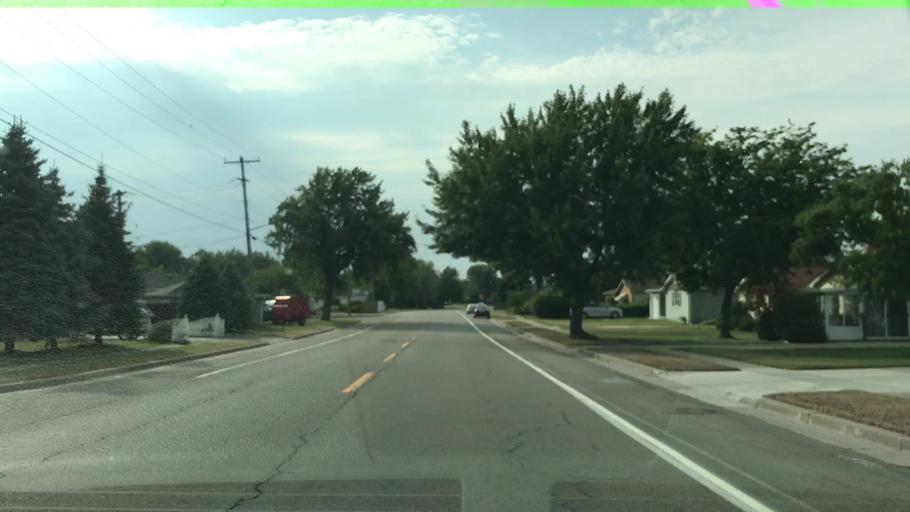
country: US
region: New York
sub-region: Erie County
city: Depew
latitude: 42.9169
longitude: -78.7114
